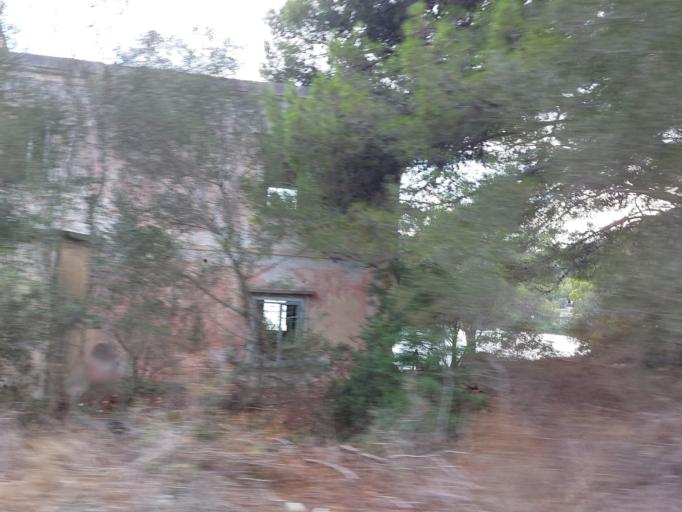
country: HR
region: Dubrovacko-Neretvanska
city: Smokvica
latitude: 42.7653
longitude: 16.8135
